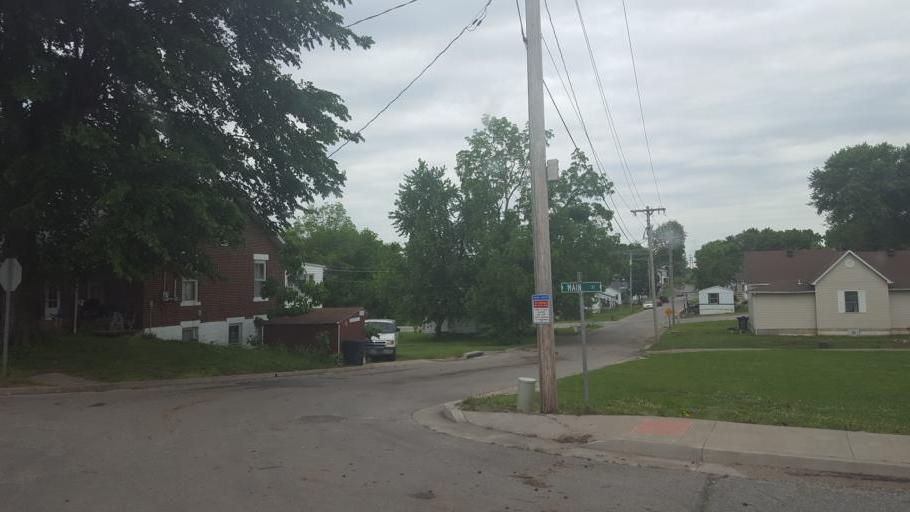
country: US
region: Missouri
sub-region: Moniteau County
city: California
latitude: 38.6362
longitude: -92.5675
